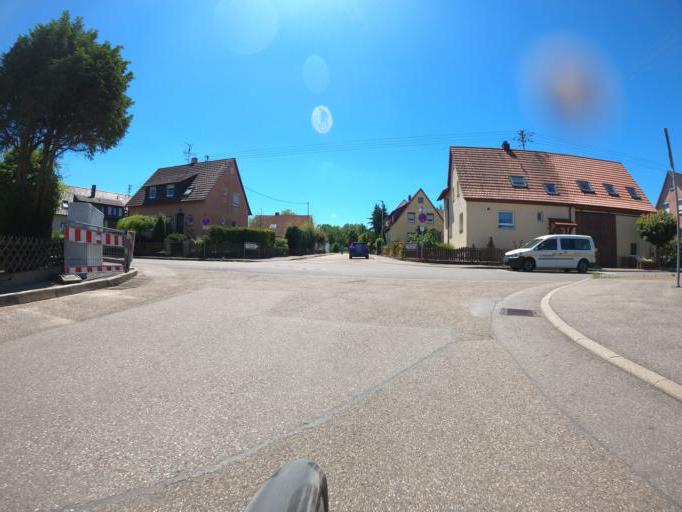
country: DE
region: Baden-Wuerttemberg
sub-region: Regierungsbezirk Stuttgart
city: Sersheim
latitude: 48.9772
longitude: 8.9867
